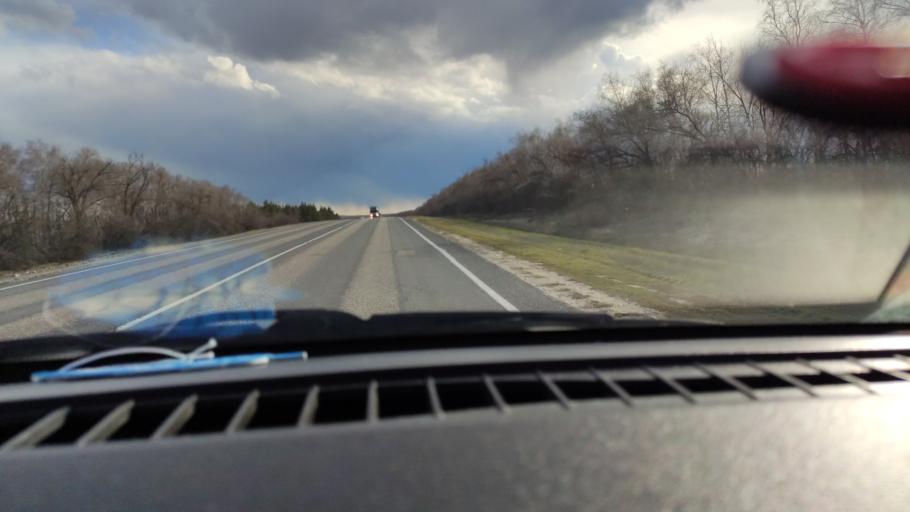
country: RU
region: Saratov
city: Sinodskoye
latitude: 51.9395
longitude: 46.5950
